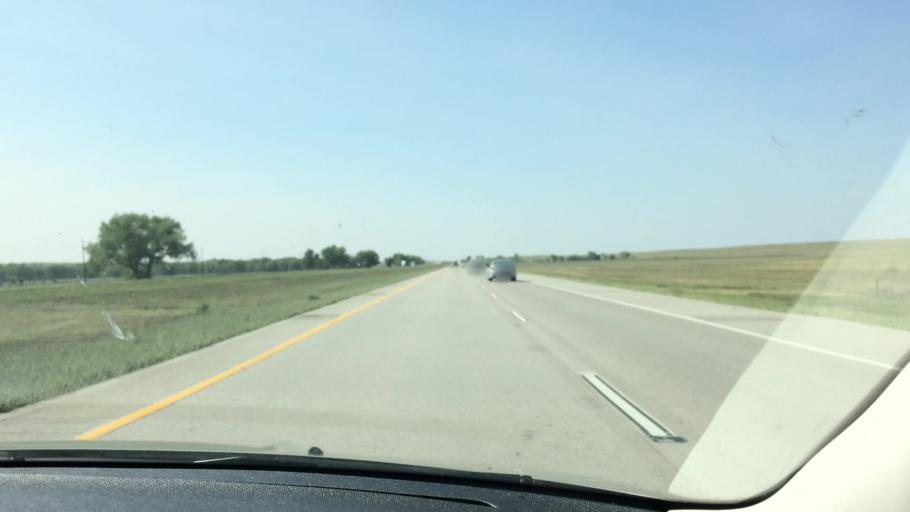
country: US
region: Colorado
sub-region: Arapahoe County
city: Byers
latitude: 39.5586
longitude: -104.0087
